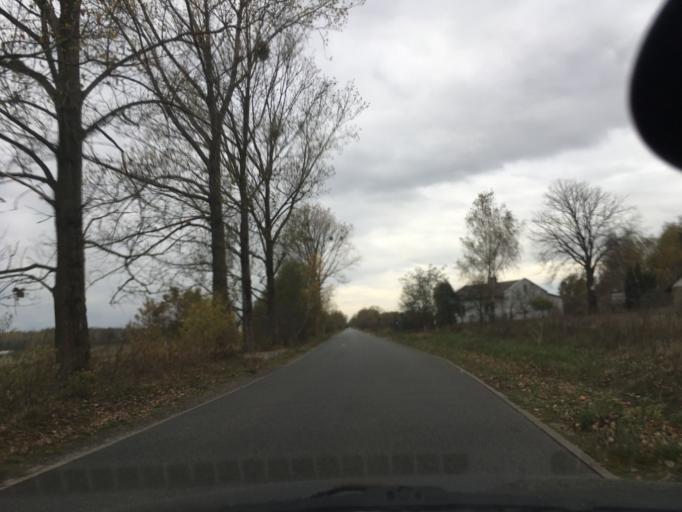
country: PL
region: Lodz Voivodeship
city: Zabia Wola
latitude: 52.0208
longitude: 20.7201
